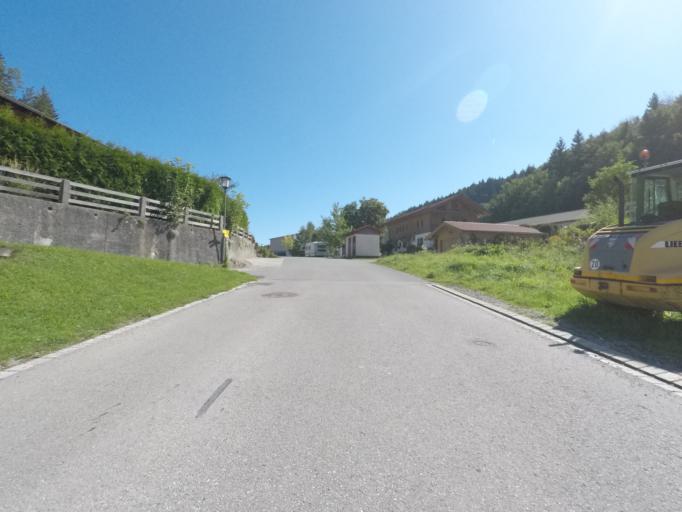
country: DE
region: Bavaria
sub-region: Upper Bavaria
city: Waakirchen
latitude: 47.7498
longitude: 11.6709
